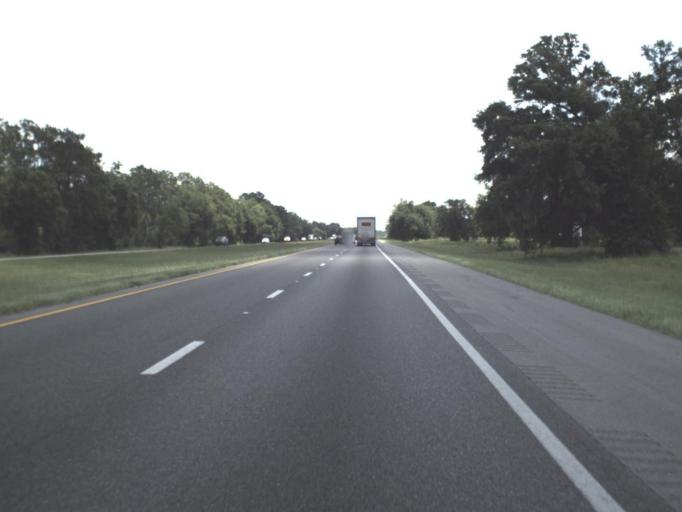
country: US
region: Florida
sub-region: Madison County
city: Madison
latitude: 30.3901
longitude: -83.3339
